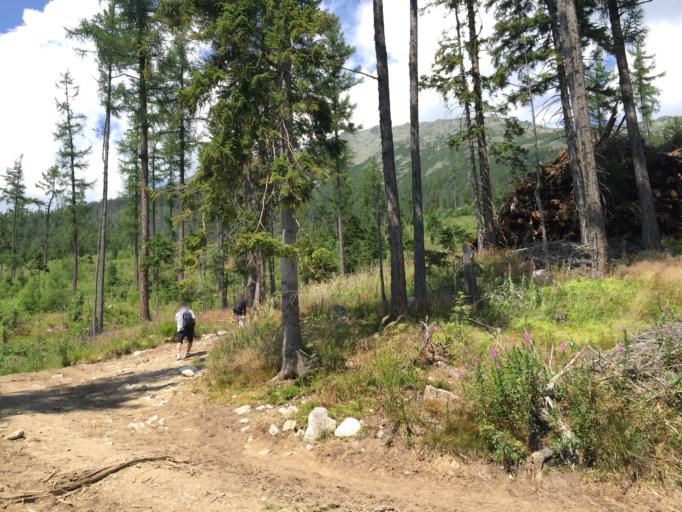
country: SK
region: Presovsky
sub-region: Okres Poprad
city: Vysoke Tatry
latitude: 49.1486
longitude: 20.2088
